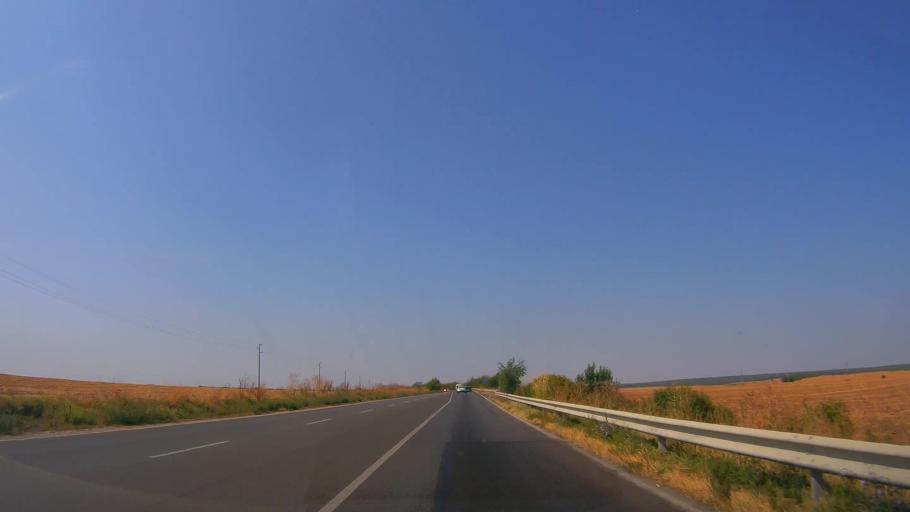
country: BG
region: Ruse
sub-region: Obshtina Vetovo
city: Senovo
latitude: 43.5630
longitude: 26.3422
